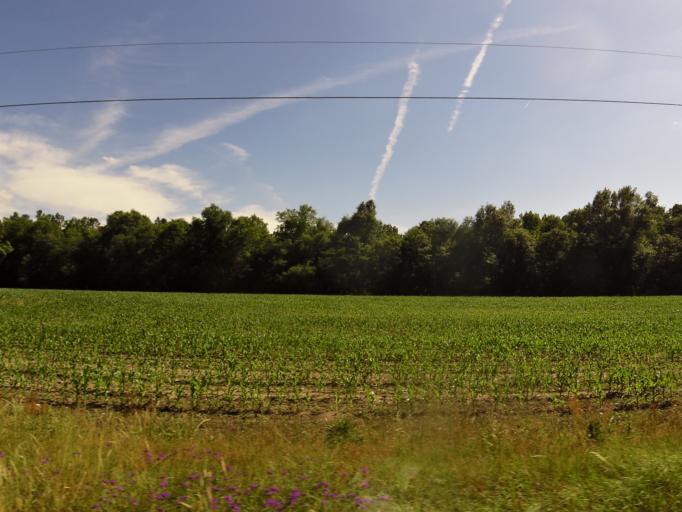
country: US
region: South Carolina
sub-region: Bamberg County
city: Denmark
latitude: 33.3398
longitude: -81.1771
